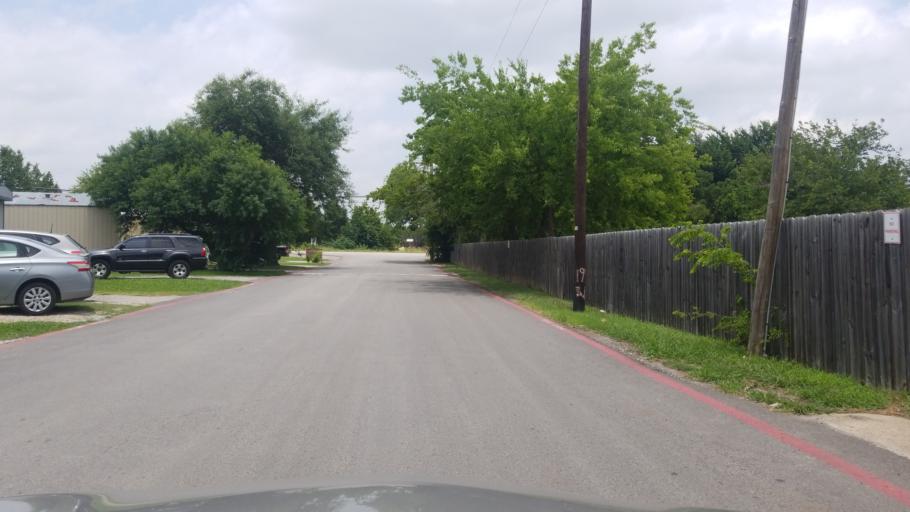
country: US
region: Texas
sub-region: Dallas County
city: Duncanville
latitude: 32.6904
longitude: -96.9125
